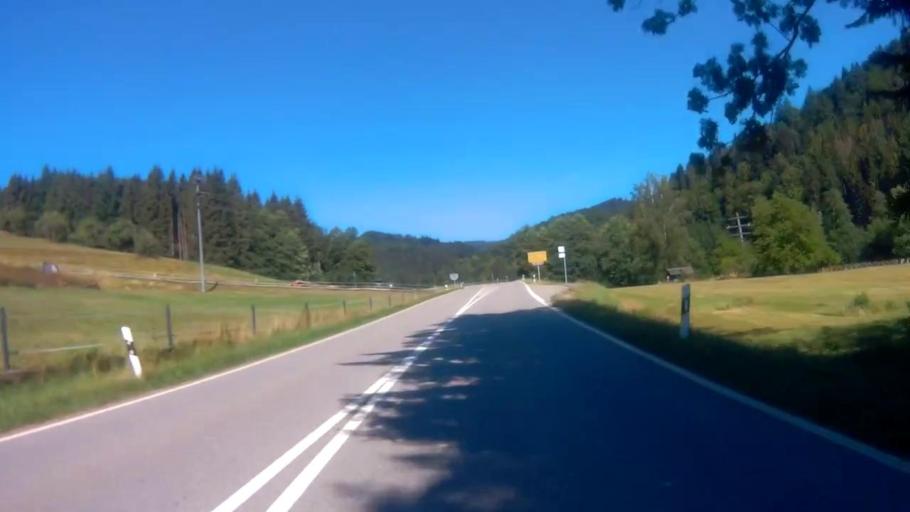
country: DE
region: Baden-Wuerttemberg
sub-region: Freiburg Region
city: Hausen
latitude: 47.7209
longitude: 7.7892
